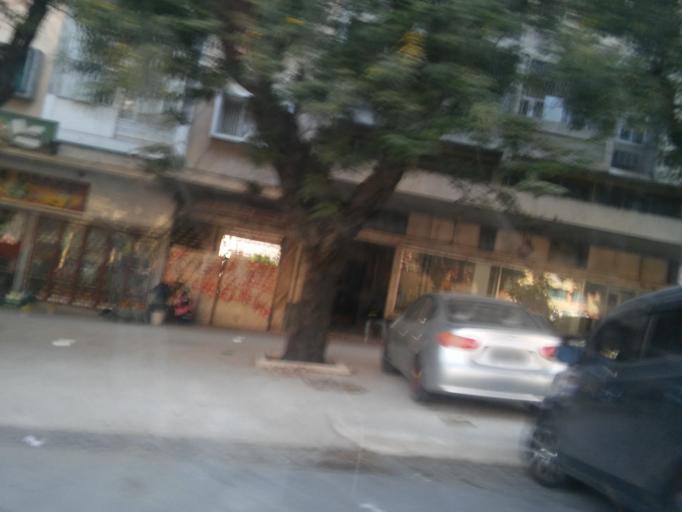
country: MZ
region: Maputo City
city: Maputo
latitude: -25.9644
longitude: 32.5722
